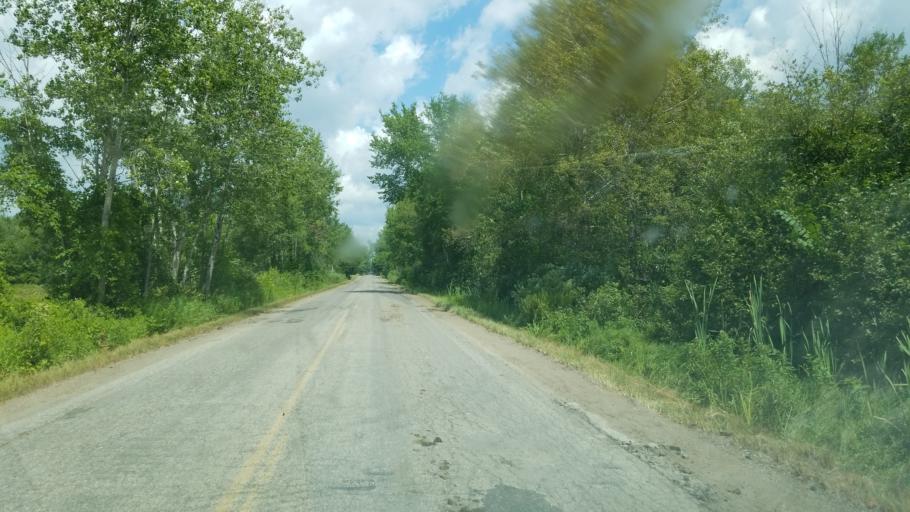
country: US
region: Michigan
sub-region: Mecosta County
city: Canadian Lakes
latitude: 43.5572
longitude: -85.3934
